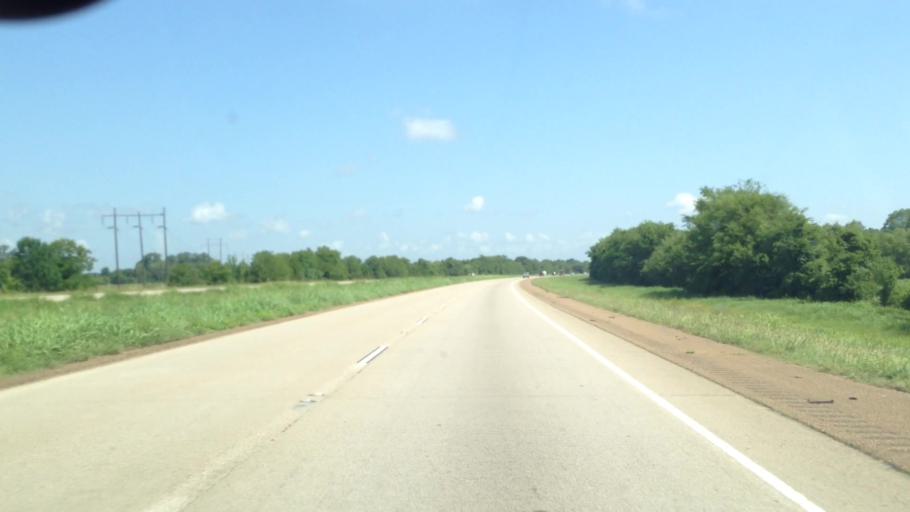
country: US
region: Louisiana
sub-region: Rapides Parish
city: Woodworth
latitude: 31.1890
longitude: -92.4727
